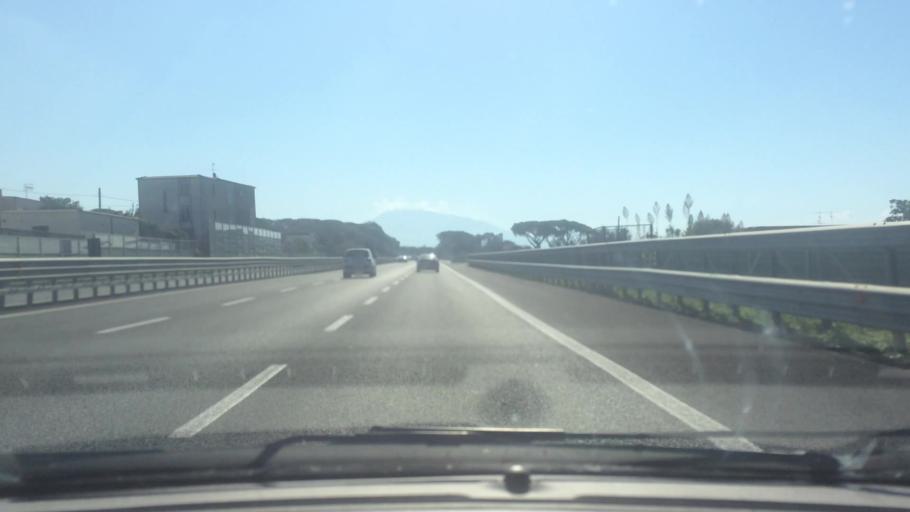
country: IT
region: Campania
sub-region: Provincia di Napoli
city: Ercolano
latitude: 40.8014
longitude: 14.3692
